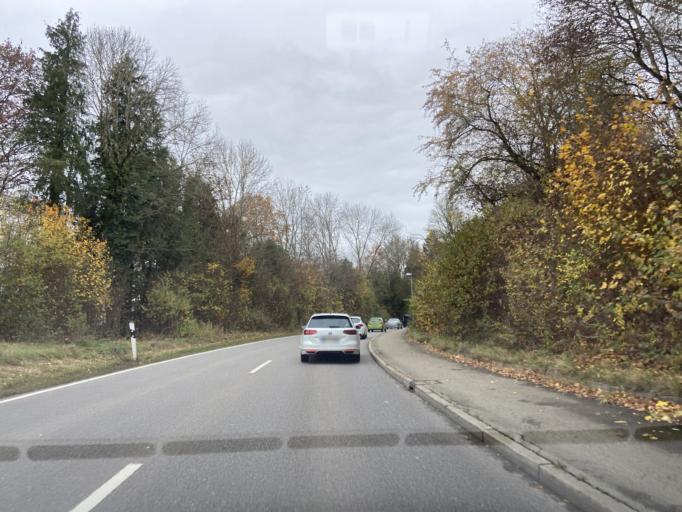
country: DE
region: Baden-Wuerttemberg
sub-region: Tuebingen Region
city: Sigmaringen
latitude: 48.0837
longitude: 9.2293
